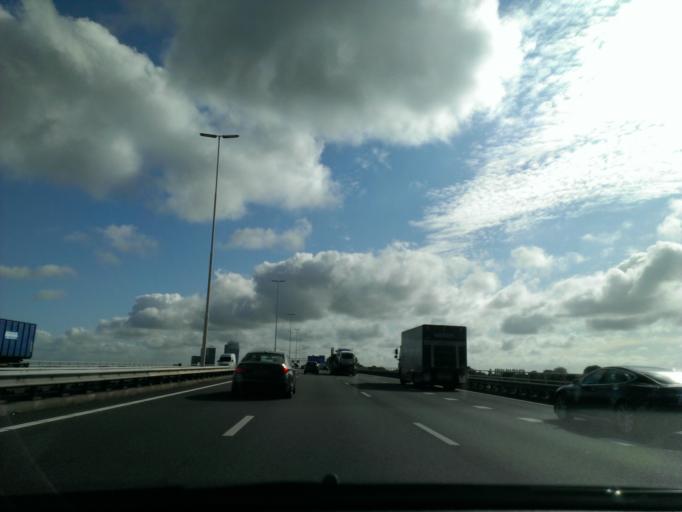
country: NL
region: Gelderland
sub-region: Gemeente Hattem
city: Hattem
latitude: 52.4979
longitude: 6.0507
